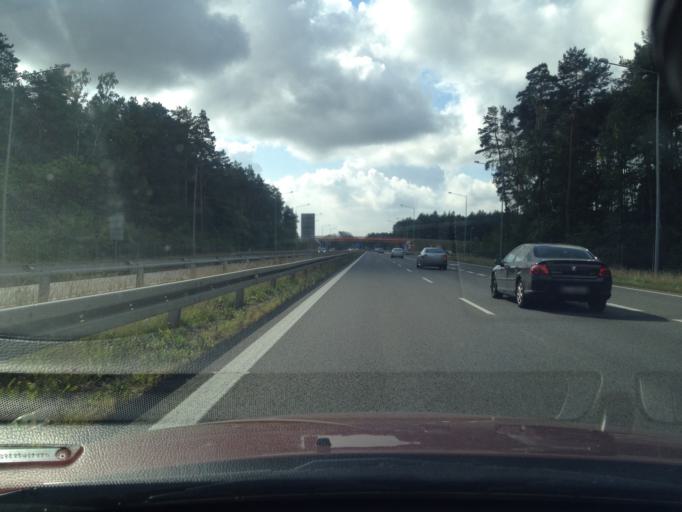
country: PL
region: West Pomeranian Voivodeship
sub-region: Powiat goleniowski
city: Goleniow
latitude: 53.6284
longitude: 14.8185
